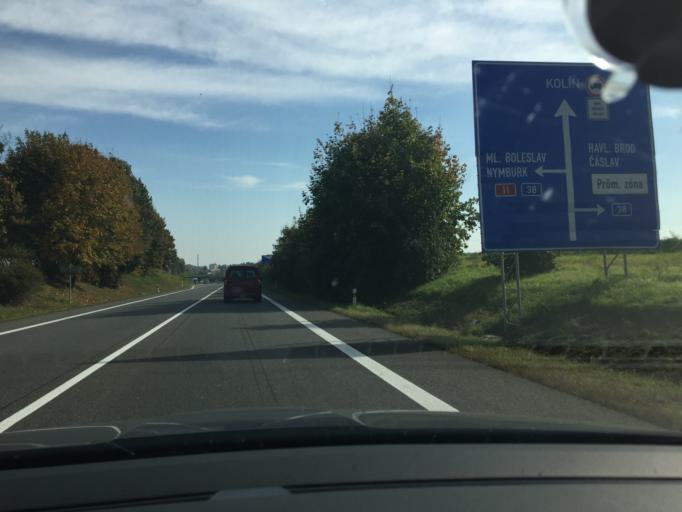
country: CZ
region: Central Bohemia
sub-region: Okres Kolin
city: Kolin
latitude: 50.0335
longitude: 15.1616
